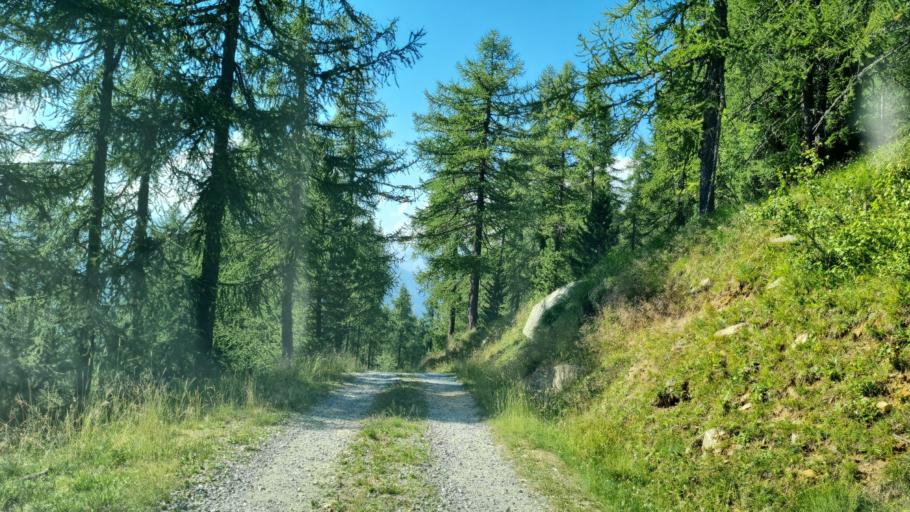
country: IT
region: Aosta Valley
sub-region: Valle d'Aosta
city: Fontainemore
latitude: 45.6210
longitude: 7.8754
